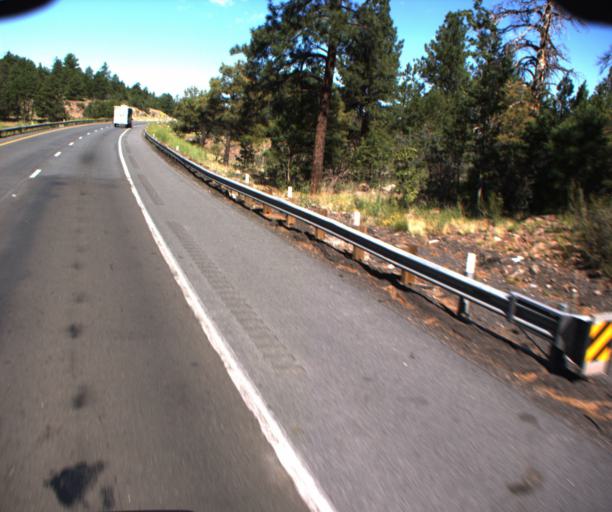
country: US
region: Arizona
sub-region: Coconino County
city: Williams
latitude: 35.2196
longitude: -112.2843
